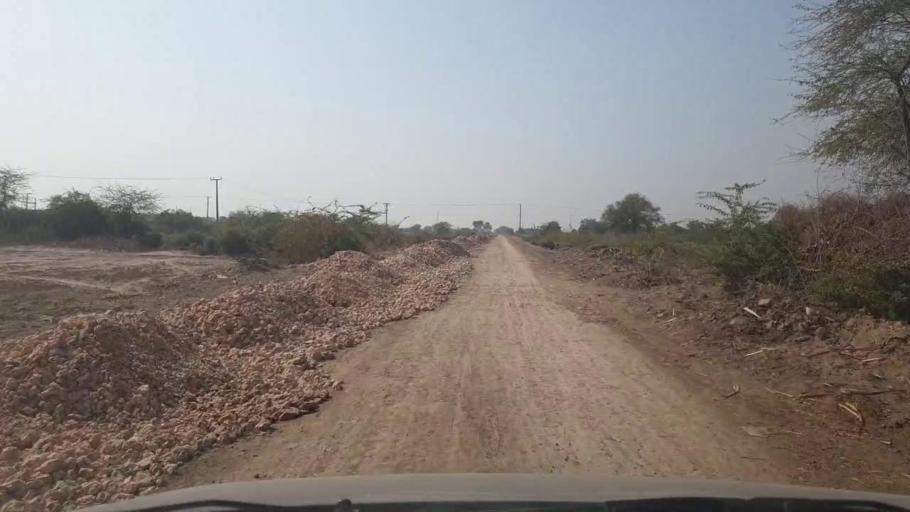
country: PK
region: Sindh
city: Mirwah Gorchani
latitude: 25.2531
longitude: 69.1118
